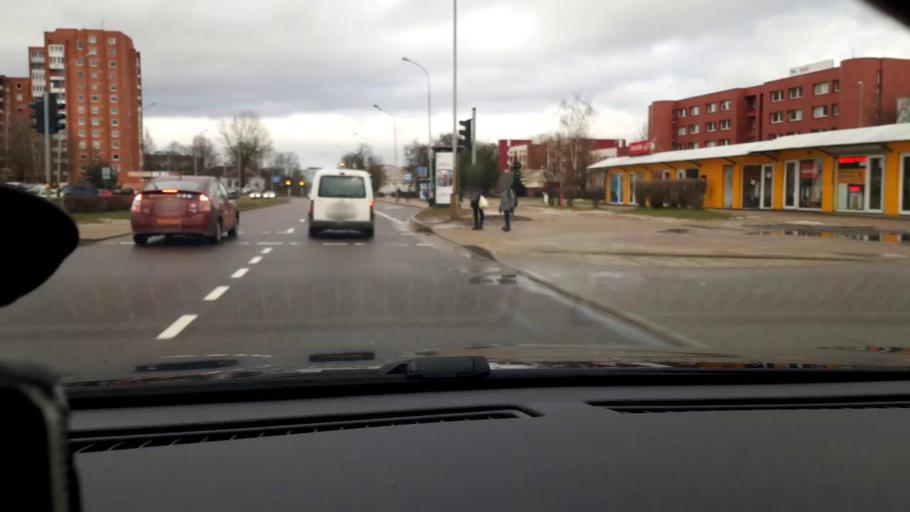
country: LT
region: Vilnius County
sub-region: Vilnius
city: Fabijoniskes
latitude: 54.7434
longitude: 25.2775
